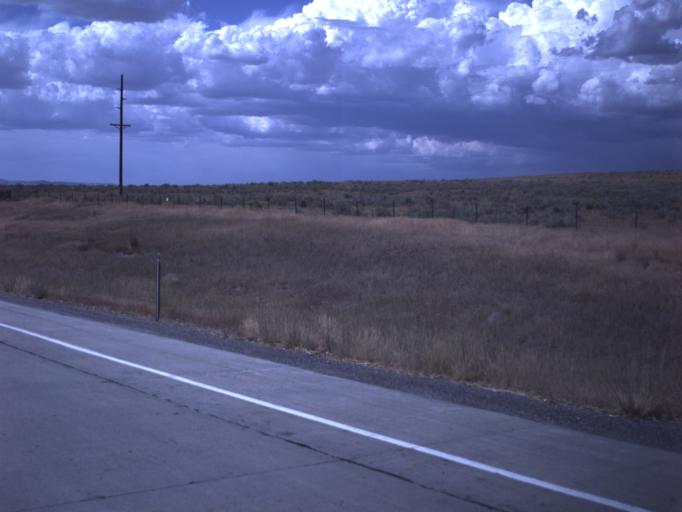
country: US
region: Utah
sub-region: Box Elder County
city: Garland
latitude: 41.8195
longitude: -112.4160
